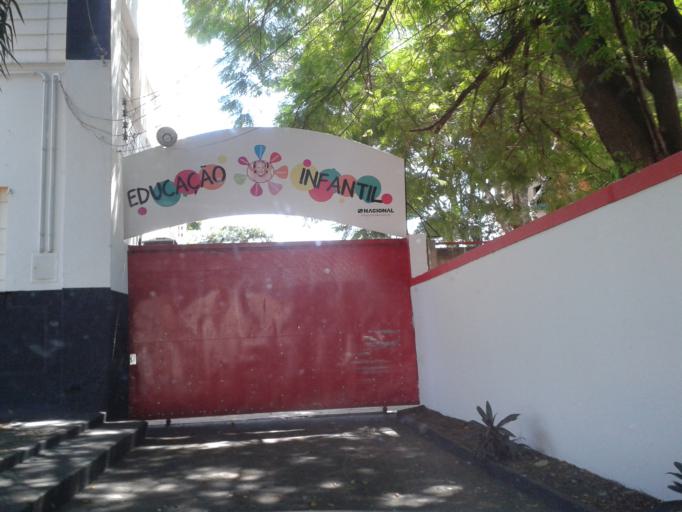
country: BR
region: Minas Gerais
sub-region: Ituiutaba
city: Ituiutaba
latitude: -18.9670
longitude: -49.4639
